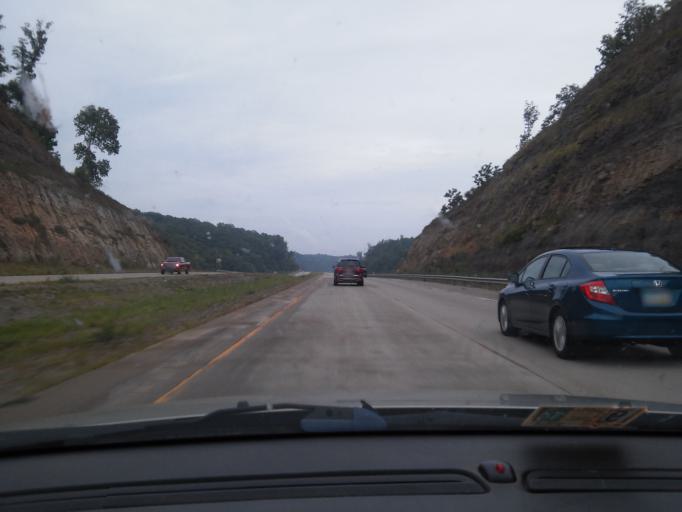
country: US
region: West Virginia
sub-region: Putnam County
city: Eleanor
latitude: 38.5312
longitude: -81.9506
